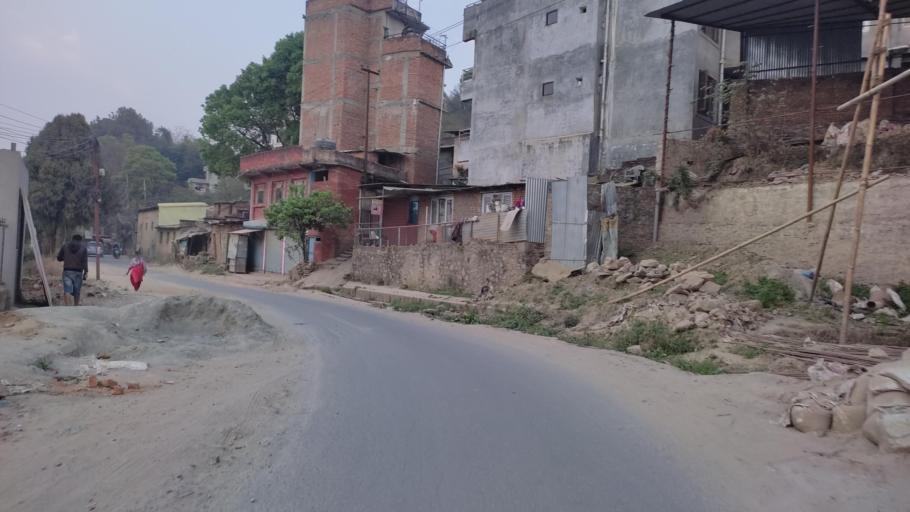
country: NP
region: Central Region
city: Kirtipur
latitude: 27.6691
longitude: 85.2866
